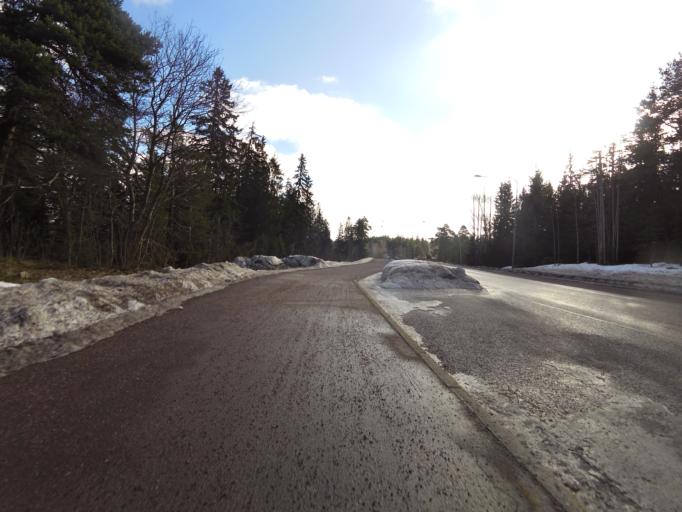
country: SE
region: Gaevleborg
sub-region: Gavle Kommun
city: Gavle
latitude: 60.6515
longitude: 17.1806
